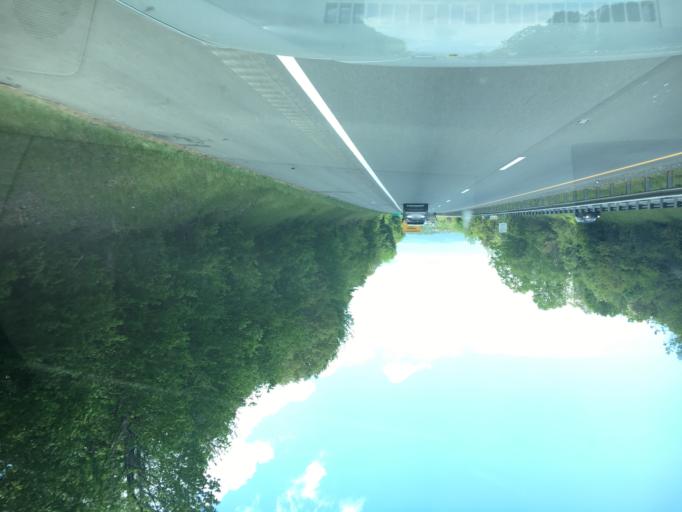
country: US
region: North Carolina
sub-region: Buncombe County
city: Weaverville
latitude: 35.6798
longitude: -82.5819
